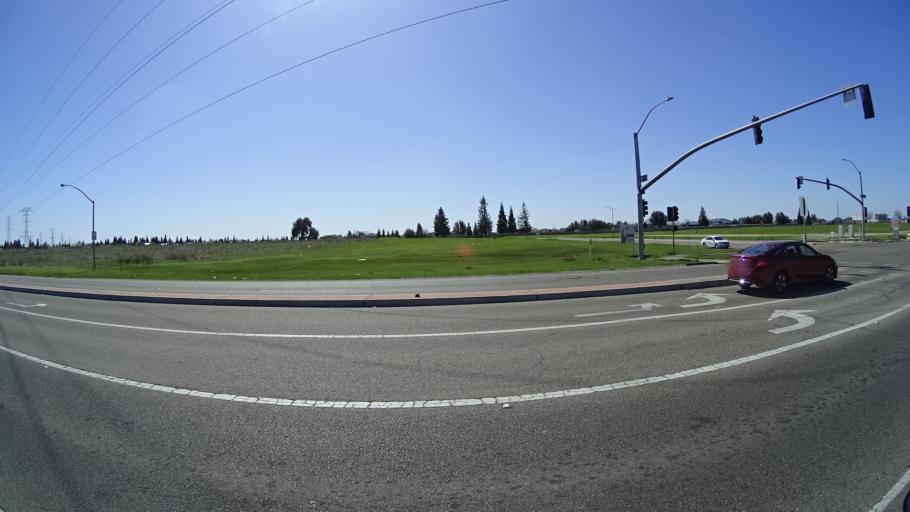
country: US
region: California
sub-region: Fresno County
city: Biola
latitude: 36.8370
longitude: -119.9012
